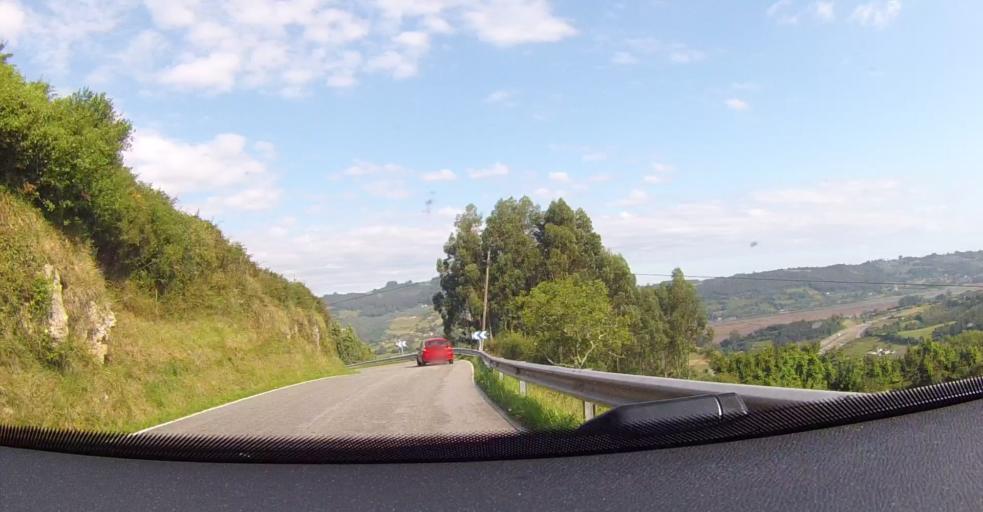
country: ES
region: Asturias
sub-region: Province of Asturias
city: Villaviciosa
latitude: 43.4863
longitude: -5.4142
